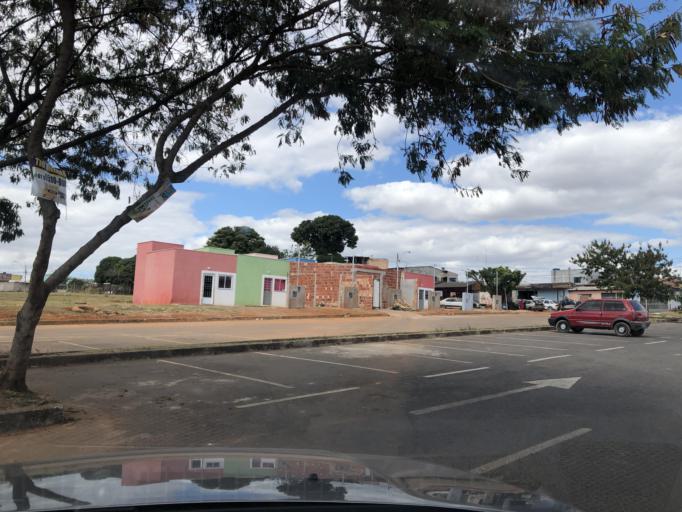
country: BR
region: Federal District
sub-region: Brasilia
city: Brasilia
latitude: -15.8835
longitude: -48.1270
